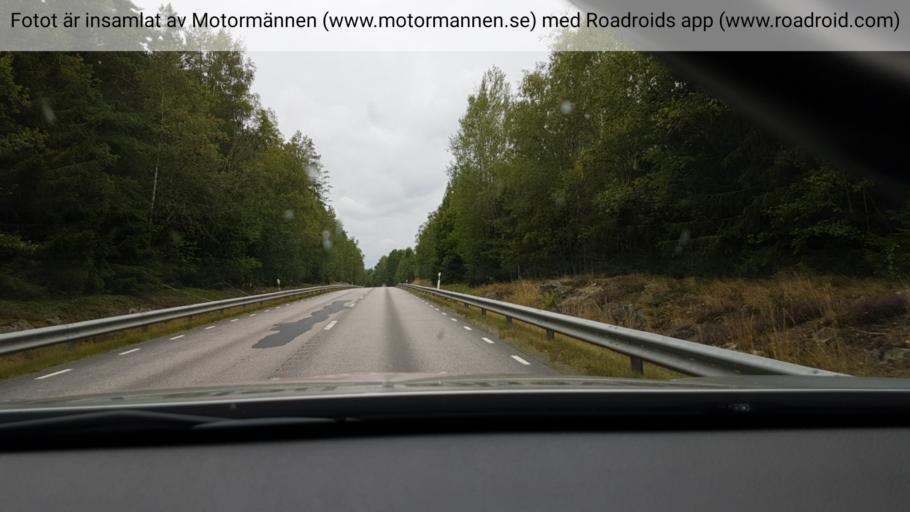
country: SE
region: Stockholm
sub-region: Vallentuna Kommun
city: Vallentuna
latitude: 59.7086
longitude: 18.0494
